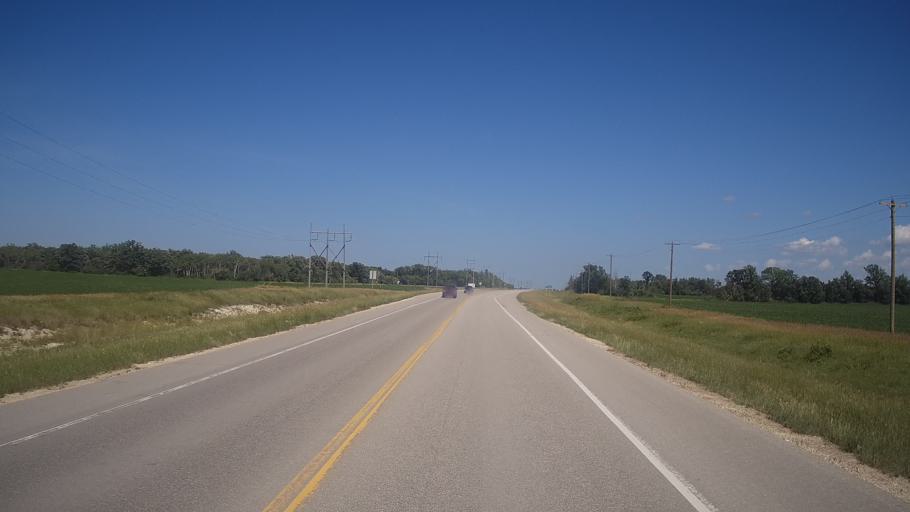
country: CA
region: Manitoba
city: Stonewall
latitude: 50.1228
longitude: -97.3406
